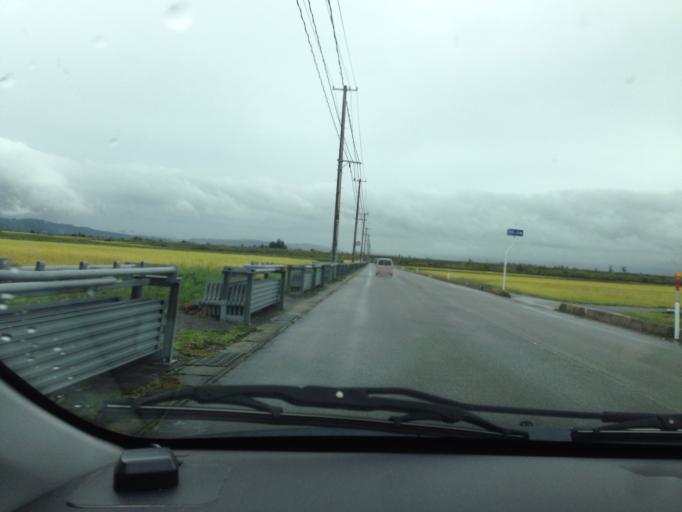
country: JP
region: Fukushima
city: Kitakata
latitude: 37.5265
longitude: 139.8200
